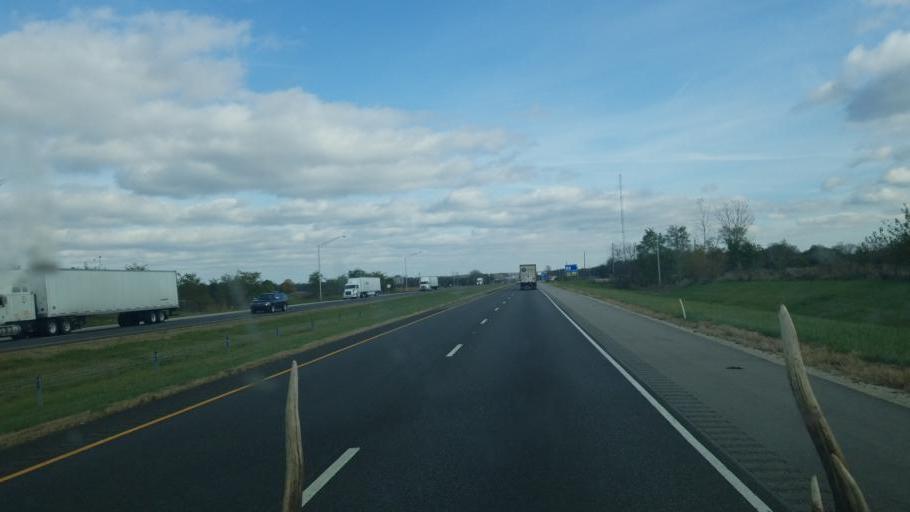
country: US
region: Indiana
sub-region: Wayne County
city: Centerville
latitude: 39.8593
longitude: -85.0200
